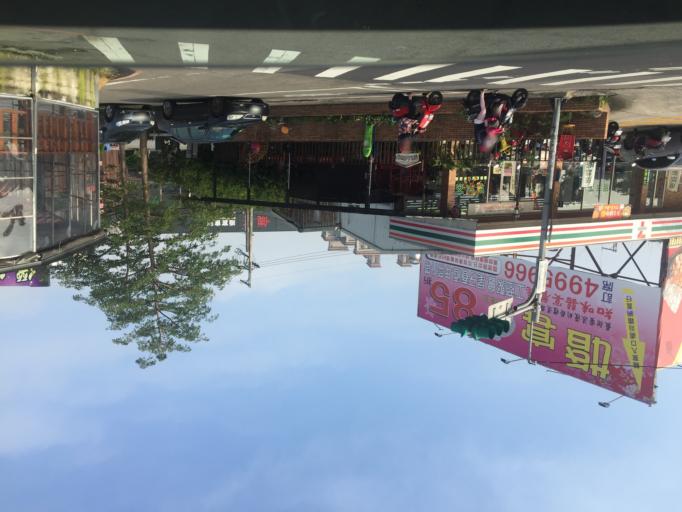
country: TW
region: Taiwan
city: Daxi
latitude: 24.8651
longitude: 121.2225
